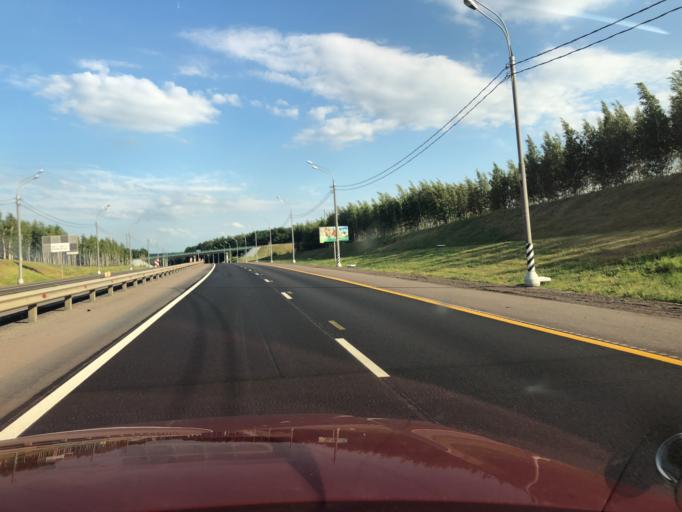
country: RU
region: Lipetsk
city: Zadonsk
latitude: 52.3888
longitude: 38.8657
